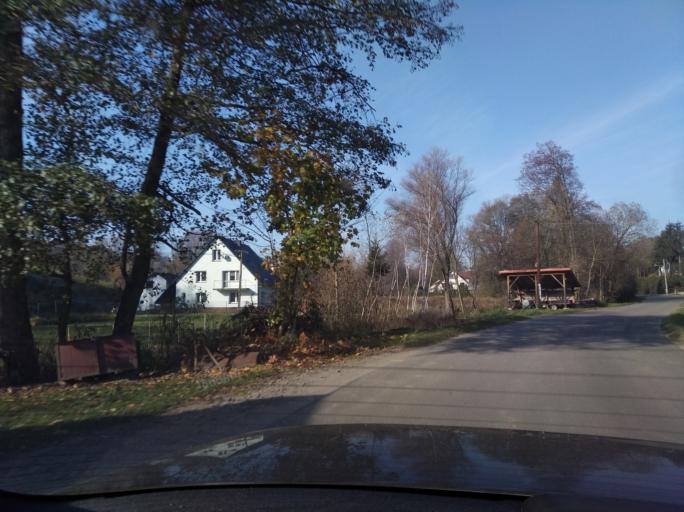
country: PL
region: Subcarpathian Voivodeship
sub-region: Powiat strzyzowski
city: Frysztak
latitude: 49.8776
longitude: 21.6156
